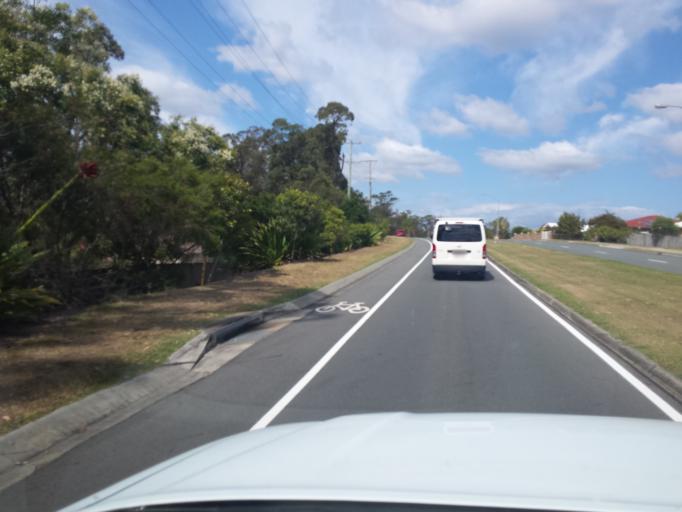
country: AU
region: Queensland
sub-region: Brisbane
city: Bridegman Downs
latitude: -27.3656
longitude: 152.9718
